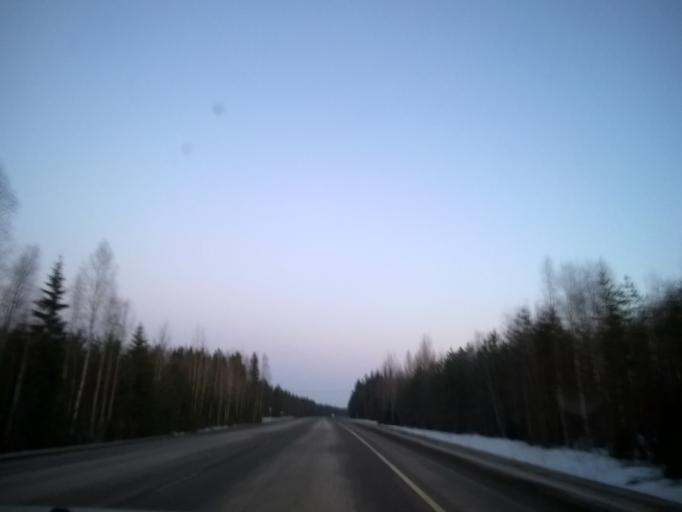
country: FI
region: Northern Ostrobothnia
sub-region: Nivala-Haapajaervi
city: Pyhaesalmi
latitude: 63.7848
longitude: 25.9289
